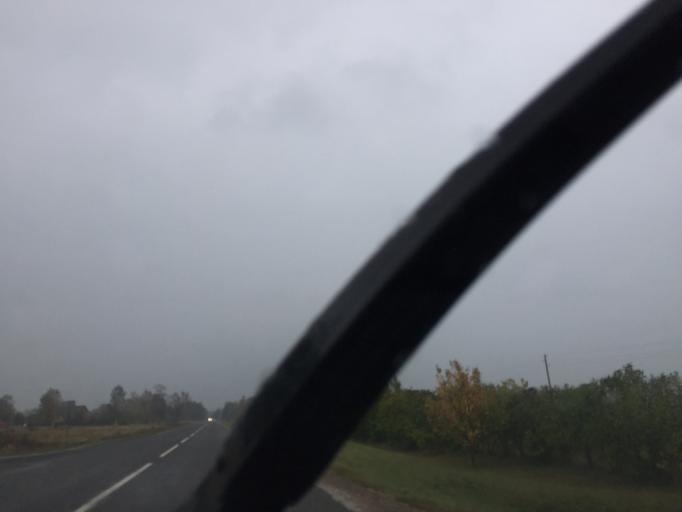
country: LV
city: Tireli
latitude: 56.6951
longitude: 23.4853
